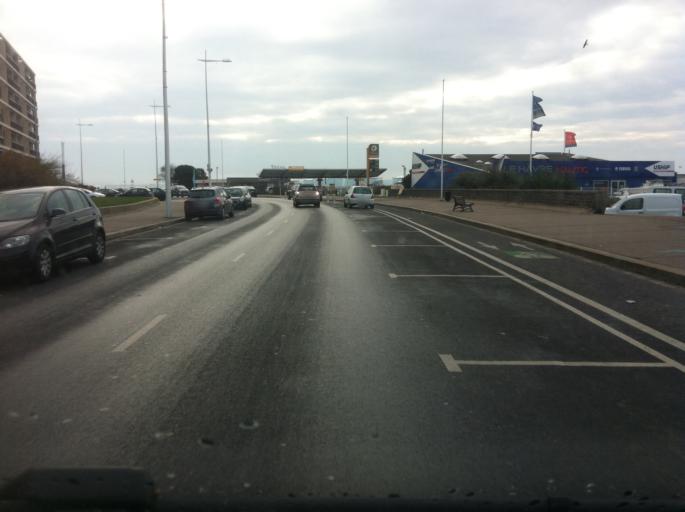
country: FR
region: Haute-Normandie
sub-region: Departement de la Seine-Maritime
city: Le Havre
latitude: 49.4874
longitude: 0.0985
